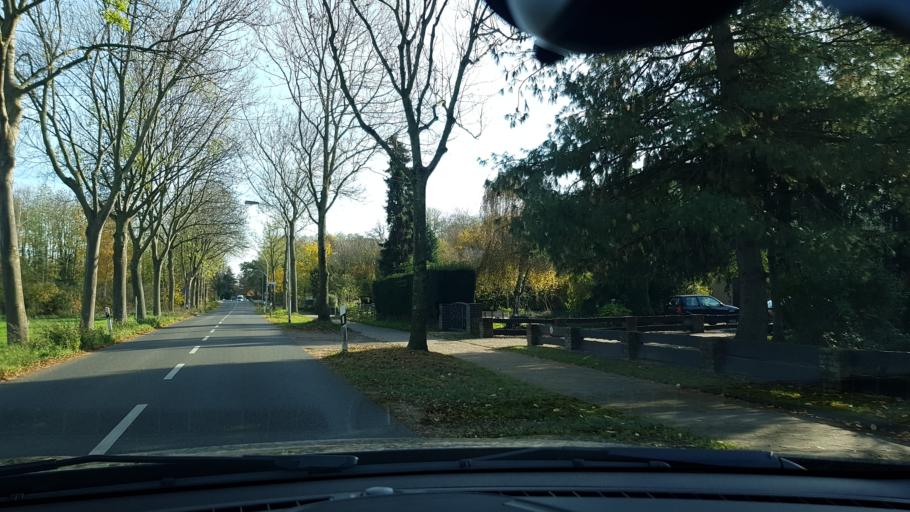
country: DE
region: North Rhine-Westphalia
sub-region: Regierungsbezirk Dusseldorf
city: Grevenbroich
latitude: 51.1057
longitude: 6.6109
